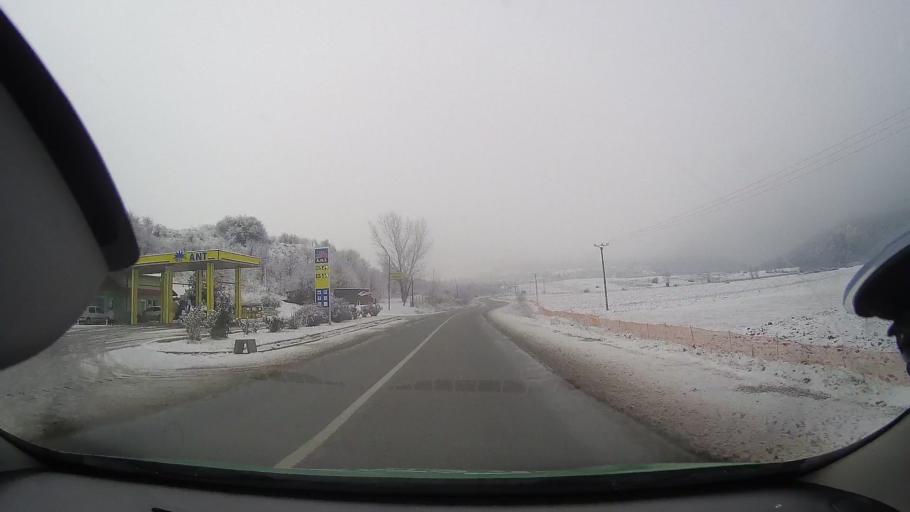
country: RO
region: Cluj
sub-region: Comuna Moldovenesti
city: Moldovenesti
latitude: 46.5110
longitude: 23.6761
